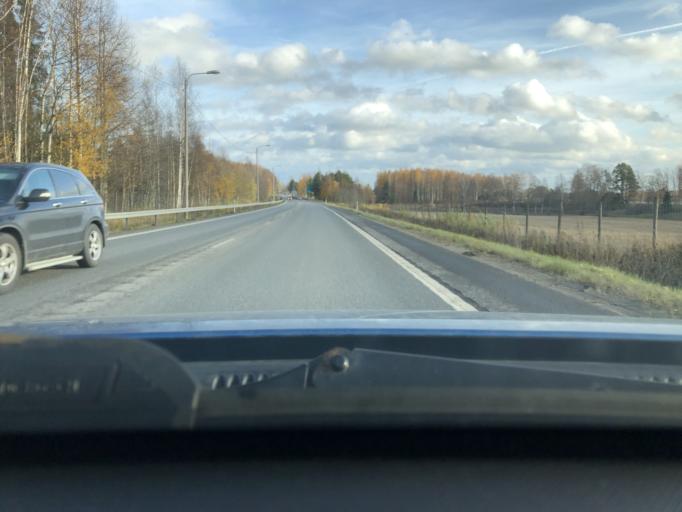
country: FI
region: Pirkanmaa
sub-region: Tampere
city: Kangasala
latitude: 61.4666
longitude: 24.0037
